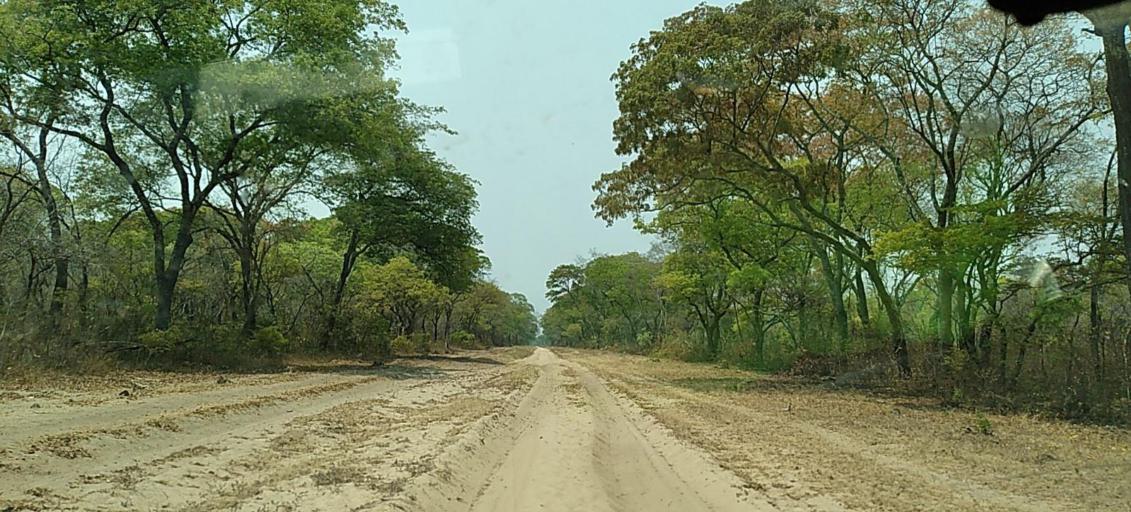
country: ZM
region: Western
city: Lukulu
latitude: -14.1348
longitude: 23.2745
